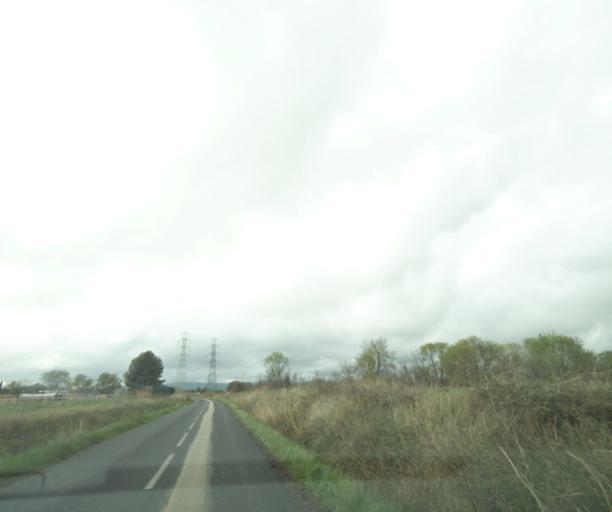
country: FR
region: Languedoc-Roussillon
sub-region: Departement de l'Herault
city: Fabregues
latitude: 43.5553
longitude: 3.7536
